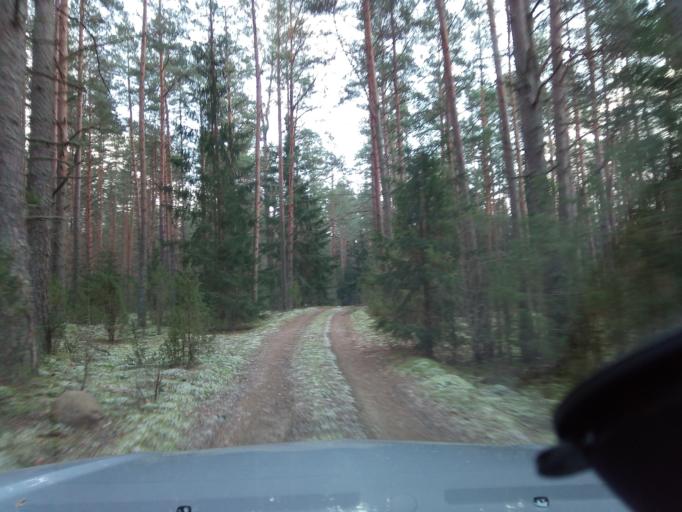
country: LT
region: Alytaus apskritis
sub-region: Alytaus rajonas
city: Daugai
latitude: 54.1088
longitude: 24.2473
